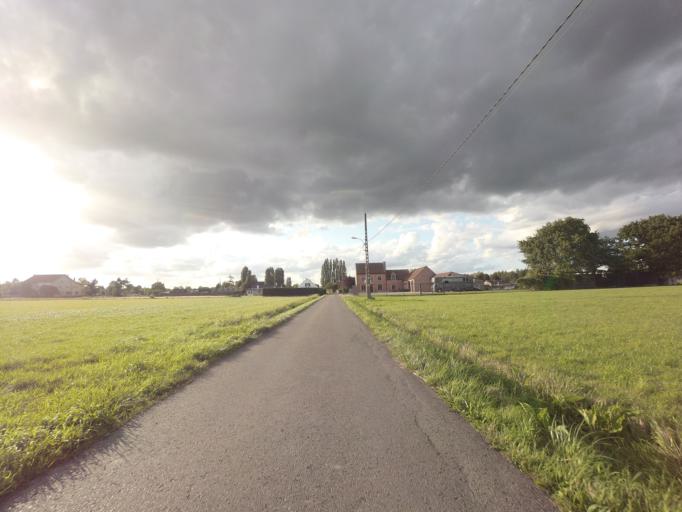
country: BE
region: Flanders
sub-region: Provincie Vlaams-Brabant
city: Londerzeel
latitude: 50.9996
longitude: 4.3202
